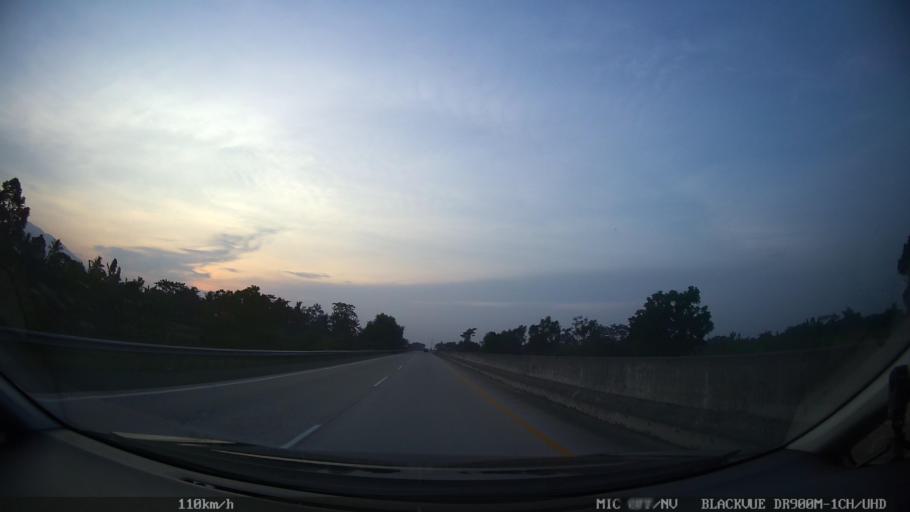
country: ID
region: Lampung
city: Pasuruan
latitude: -5.7456
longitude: 105.7000
